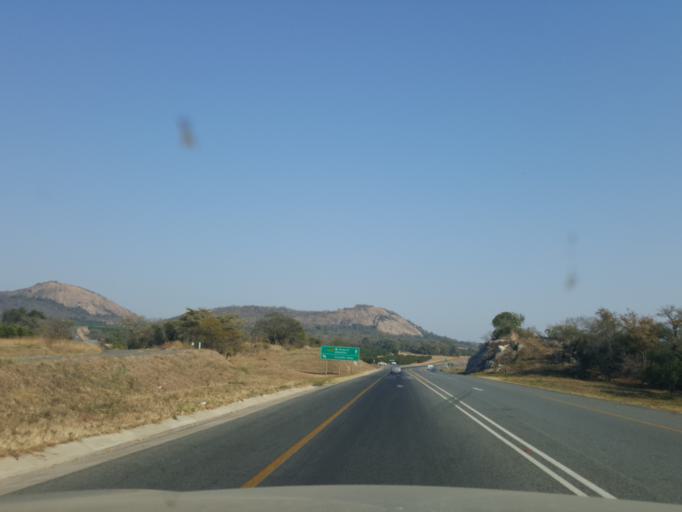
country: ZA
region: Mpumalanga
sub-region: Ehlanzeni District
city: Nelspruit
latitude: -25.4692
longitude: 31.0811
